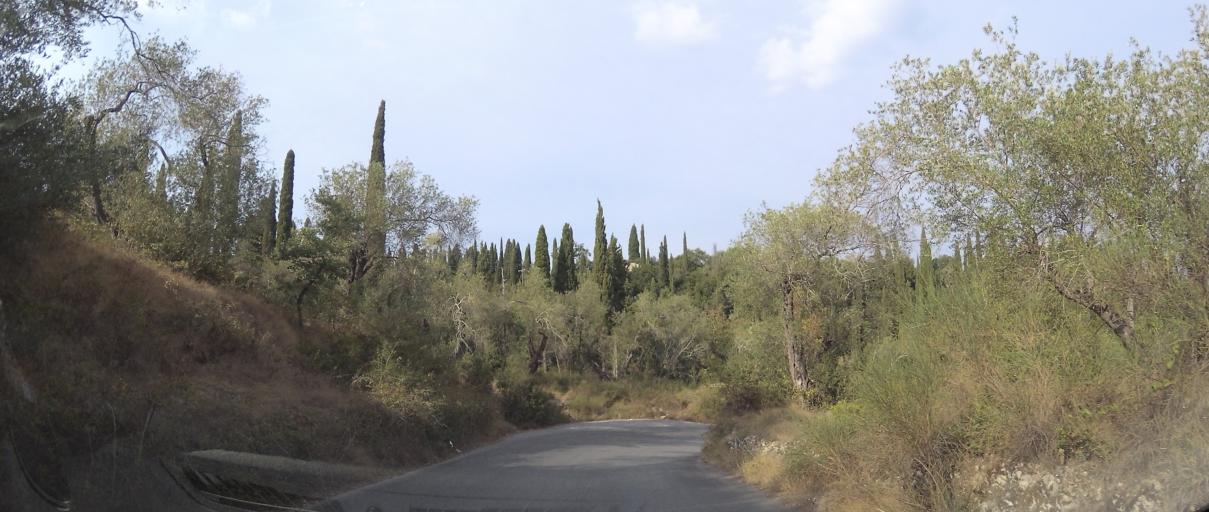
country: GR
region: Ionian Islands
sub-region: Nomos Kerkyras
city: Kynopiastes
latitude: 39.5644
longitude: 19.8706
